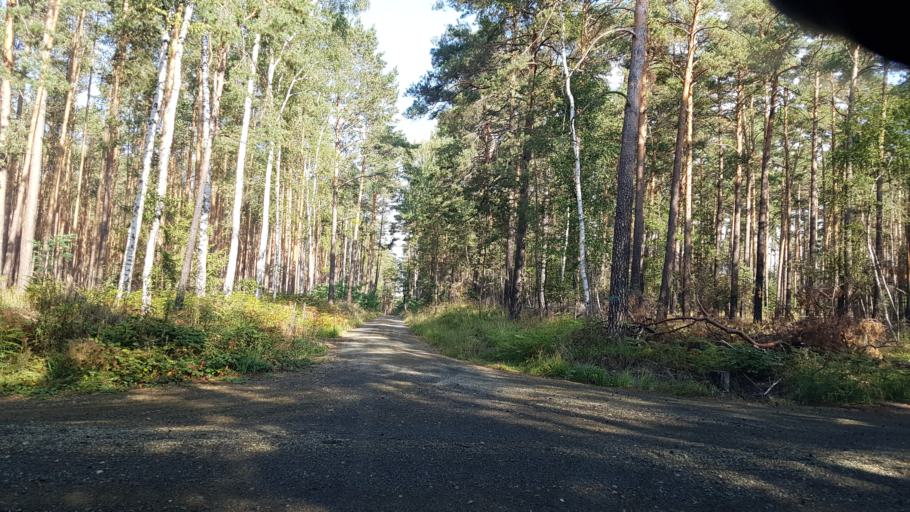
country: DE
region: Brandenburg
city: Plessa
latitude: 51.5184
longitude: 13.6398
